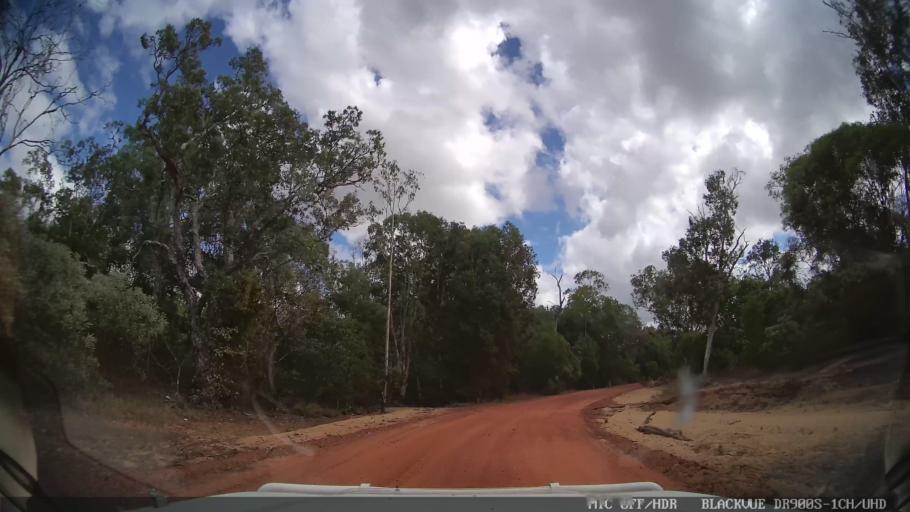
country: AU
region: Queensland
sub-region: Cook
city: Cooktown
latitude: -15.3037
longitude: 144.6165
